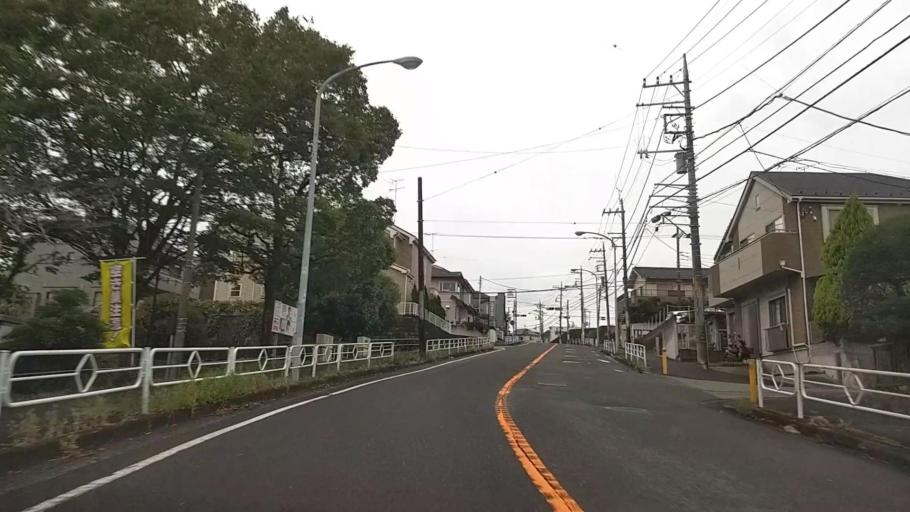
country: JP
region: Kanagawa
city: Kamakura
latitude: 35.3890
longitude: 139.5788
